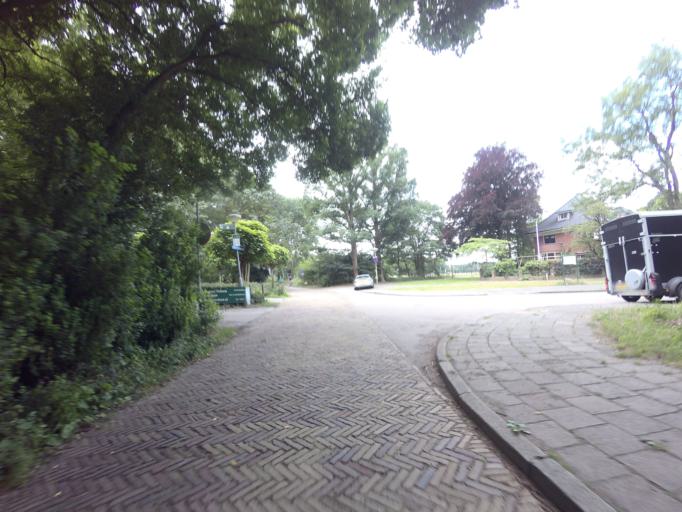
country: NL
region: North Holland
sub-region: Gemeente Velsen
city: Velsen-Zuid
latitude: 52.4556
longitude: 4.6406
